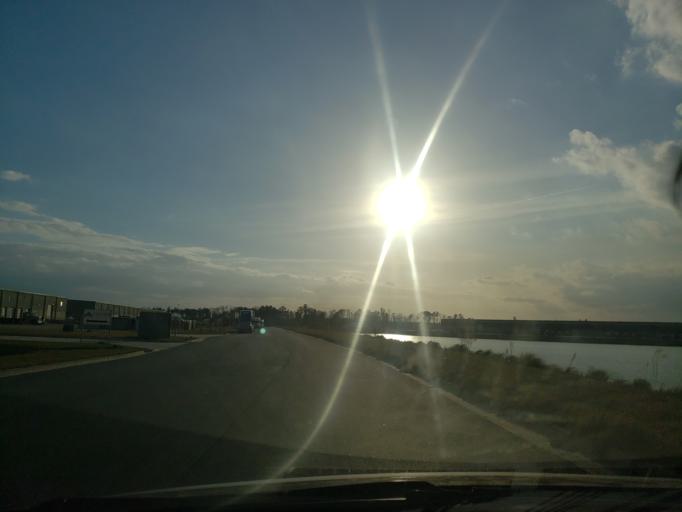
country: US
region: Georgia
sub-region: Chatham County
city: Bloomingdale
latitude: 32.1615
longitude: -81.2710
